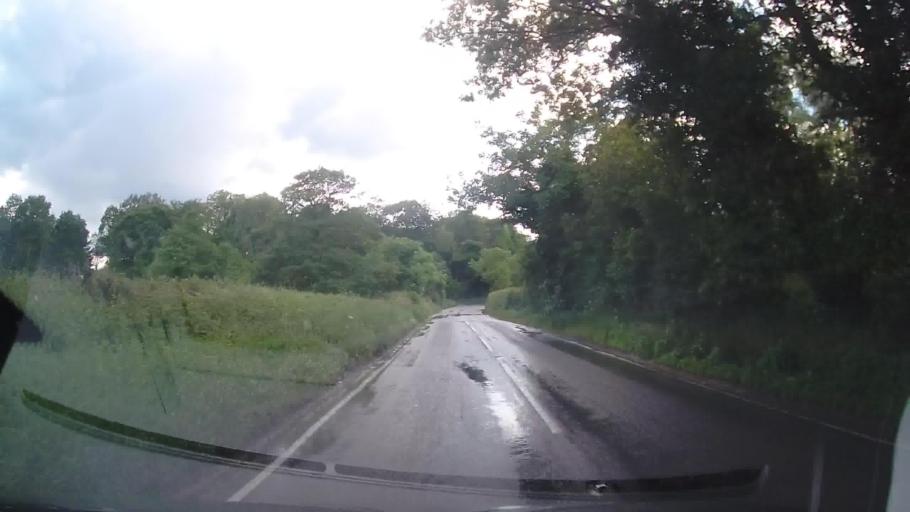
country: GB
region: England
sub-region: Shropshire
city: Berrington
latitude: 52.6778
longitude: -2.6503
